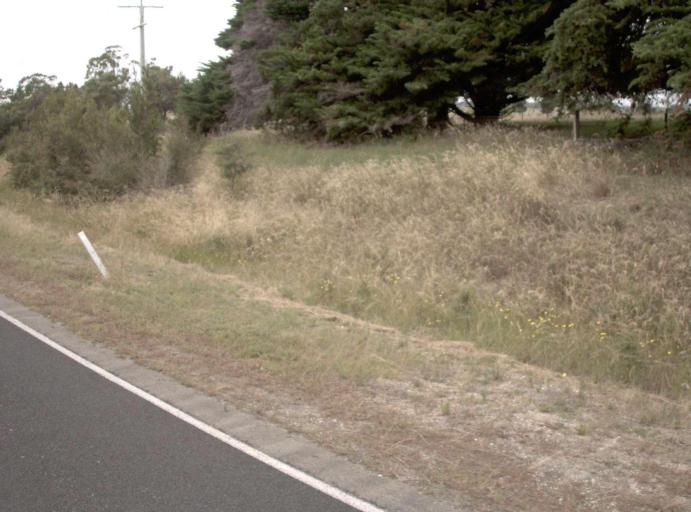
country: AU
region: Victoria
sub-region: Wellington
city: Sale
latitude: -38.1972
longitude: 147.3025
